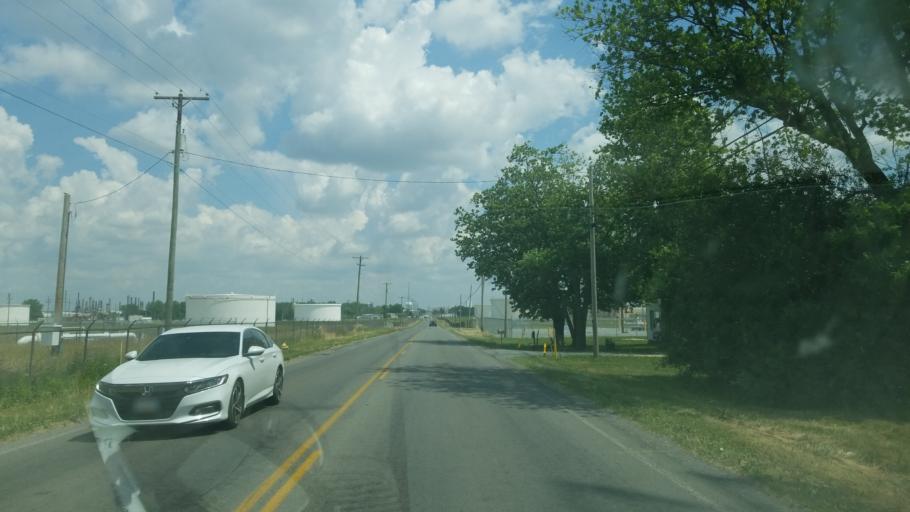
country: US
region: Ohio
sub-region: Allen County
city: Fort Shawnee
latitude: 40.7014
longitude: -84.1217
